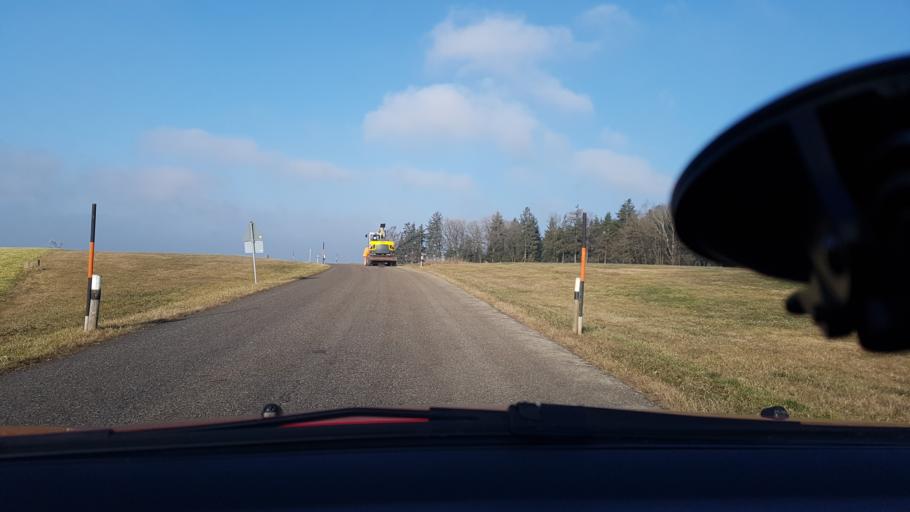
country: DE
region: Bavaria
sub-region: Lower Bavaria
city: Wittibreut
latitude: 48.3164
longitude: 13.0325
